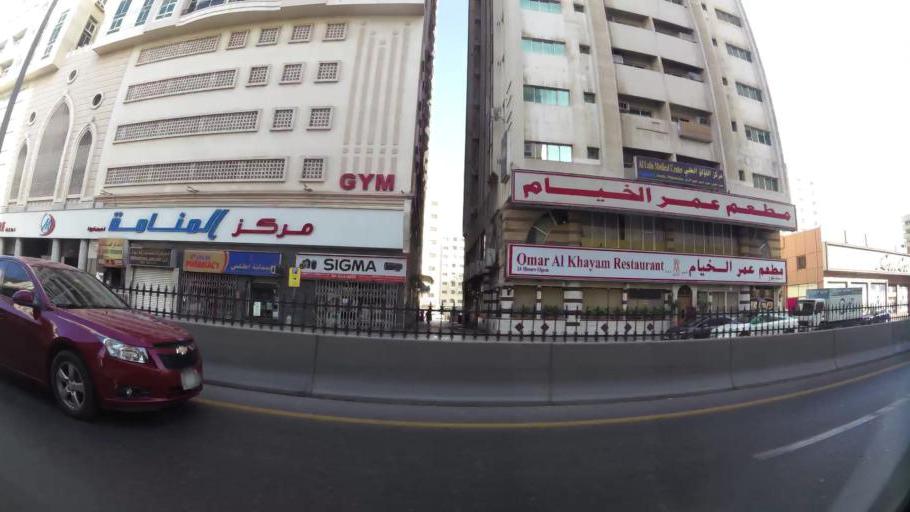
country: AE
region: Ash Shariqah
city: Sharjah
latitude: 25.3639
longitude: 55.3922
